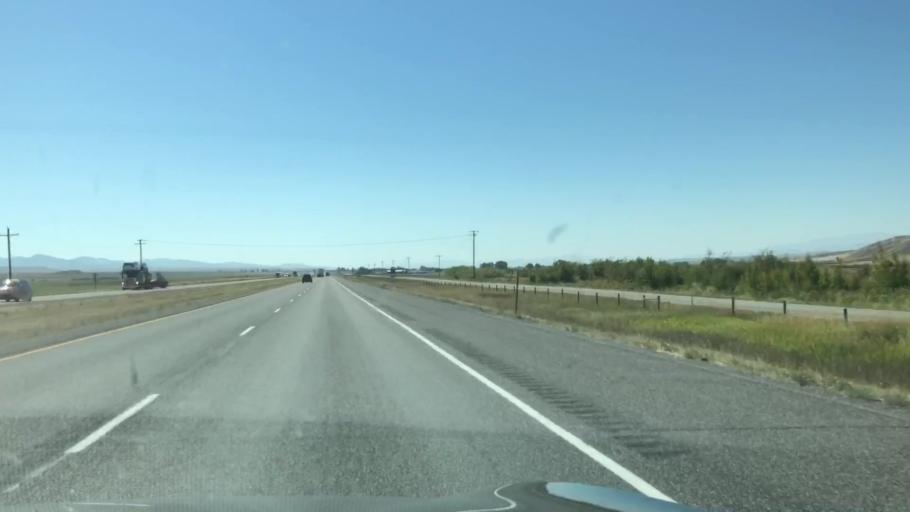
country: US
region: Montana
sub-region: Powell County
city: Deer Lodge
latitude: 46.4555
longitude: -112.7221
